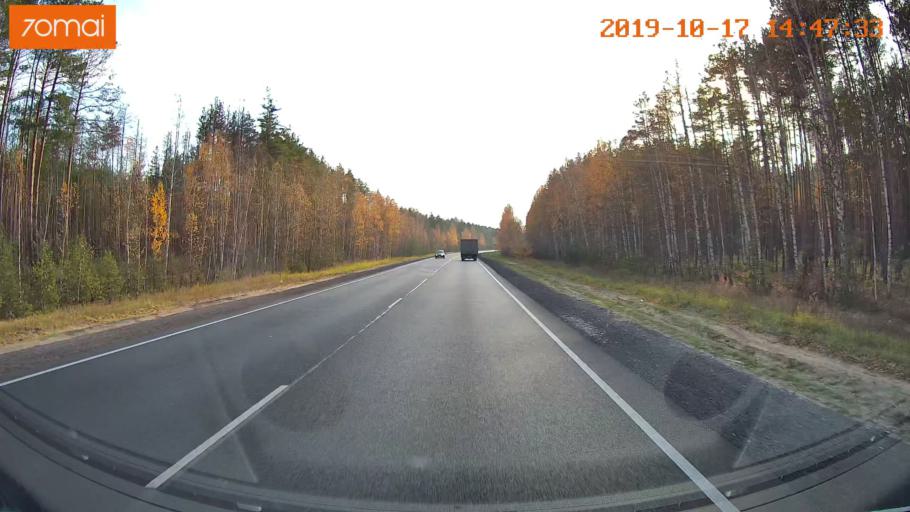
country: RU
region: Rjazan
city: Solotcha
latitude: 54.7700
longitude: 39.8597
